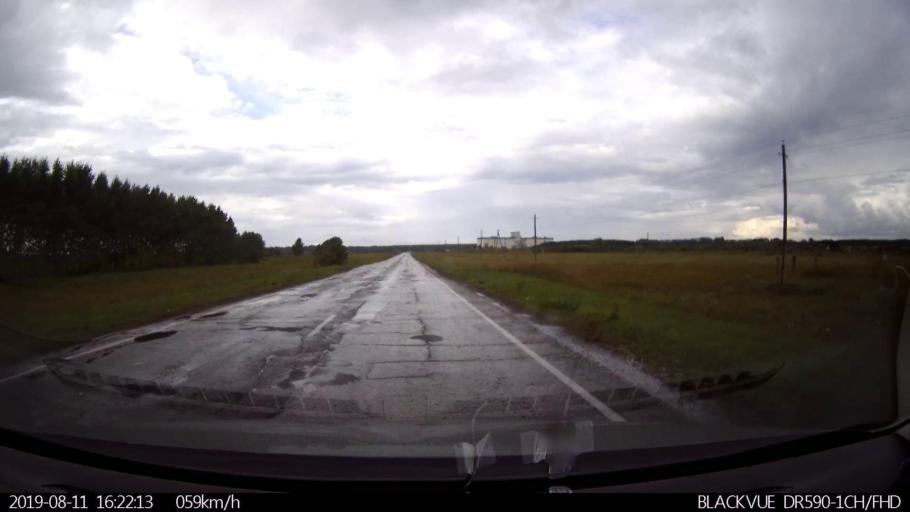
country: RU
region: Ulyanovsk
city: Mayna
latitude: 54.0861
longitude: 47.5940
